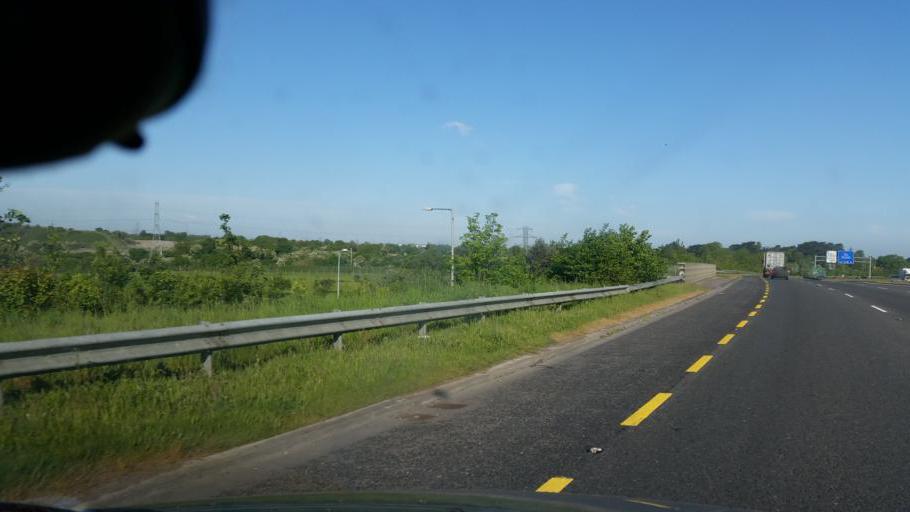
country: IE
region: Leinster
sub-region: Dublin City
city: Finglas
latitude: 53.4194
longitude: -6.3227
